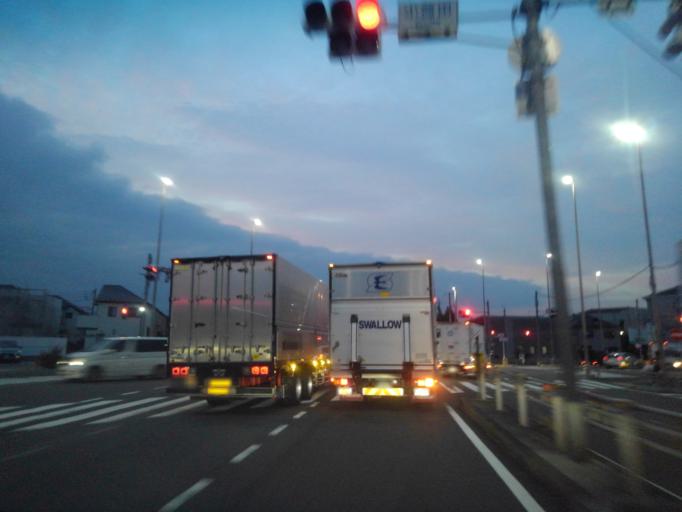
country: JP
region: Tokyo
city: Fussa
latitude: 35.7138
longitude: 139.3386
